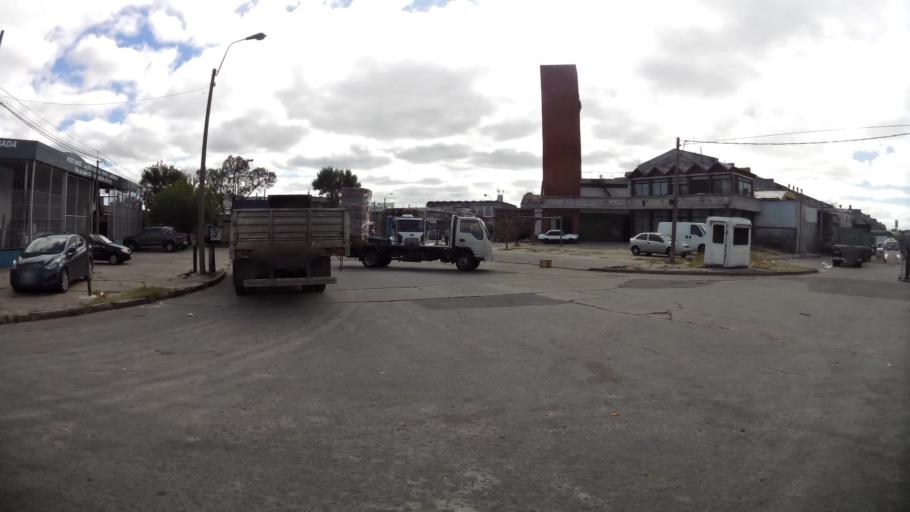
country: UY
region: Montevideo
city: Montevideo
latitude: -34.8716
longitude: -56.1563
